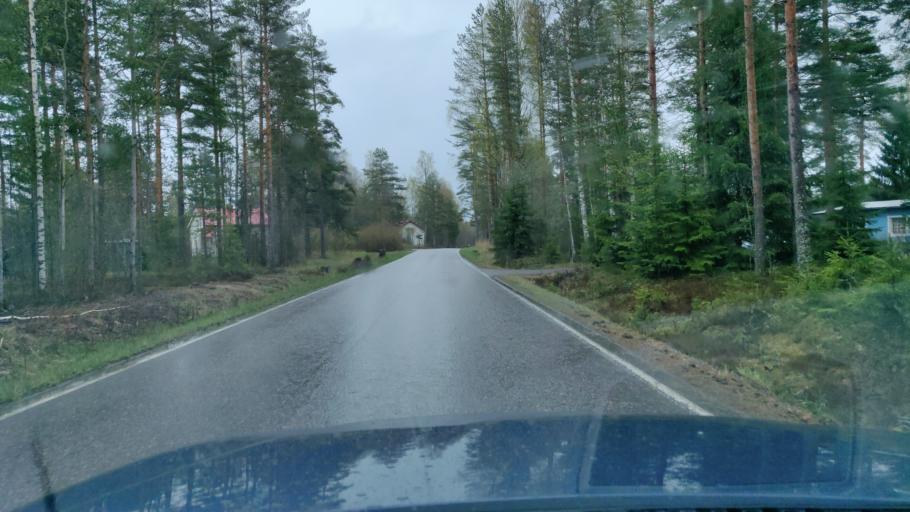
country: FI
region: Uusimaa
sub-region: Helsinki
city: Nurmijaervi
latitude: 60.4998
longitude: 24.6964
